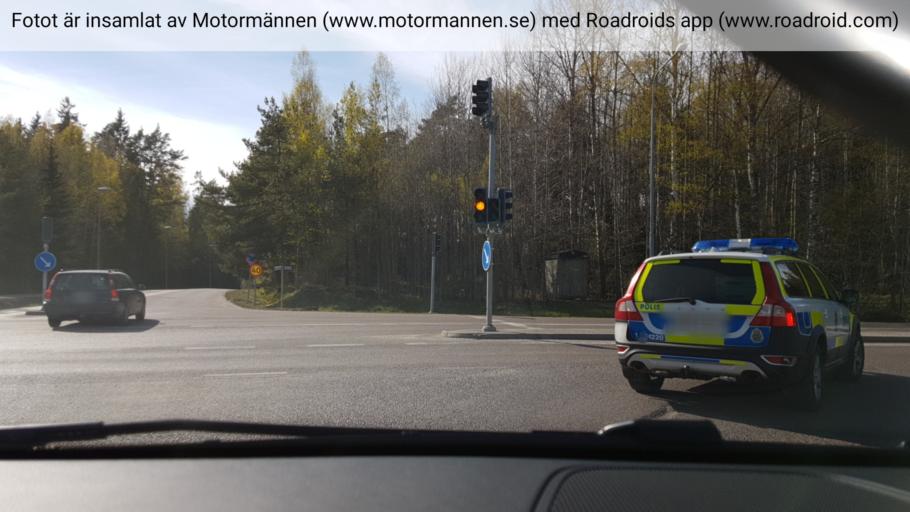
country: SE
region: Stockholm
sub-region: Botkyrka Kommun
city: Tumba
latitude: 59.1830
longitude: 17.8155
